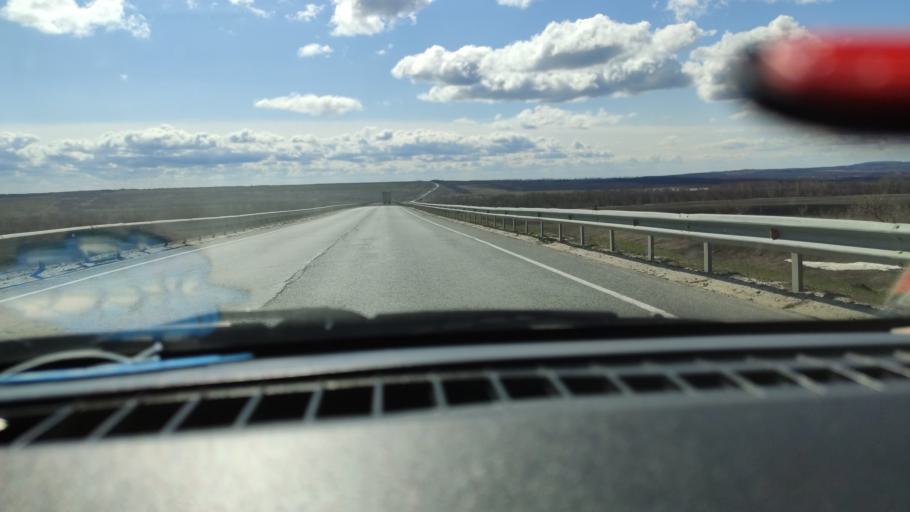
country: RU
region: Saratov
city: Dukhovnitskoye
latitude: 52.7510
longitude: 48.2482
